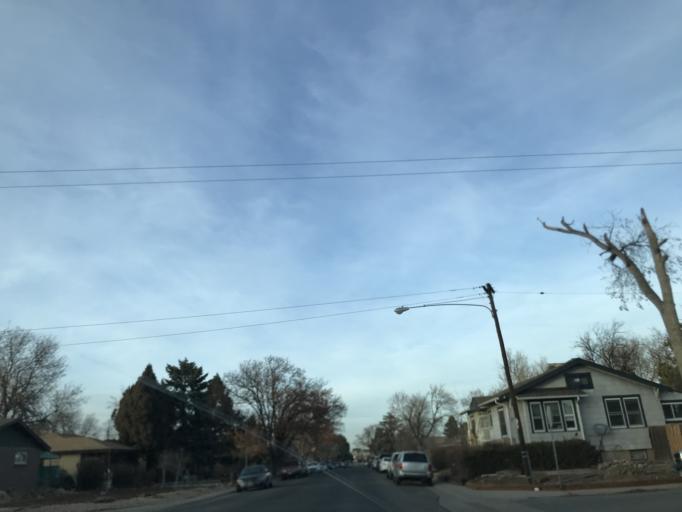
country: US
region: Colorado
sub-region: Adams County
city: Aurora
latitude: 39.7491
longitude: -104.8658
